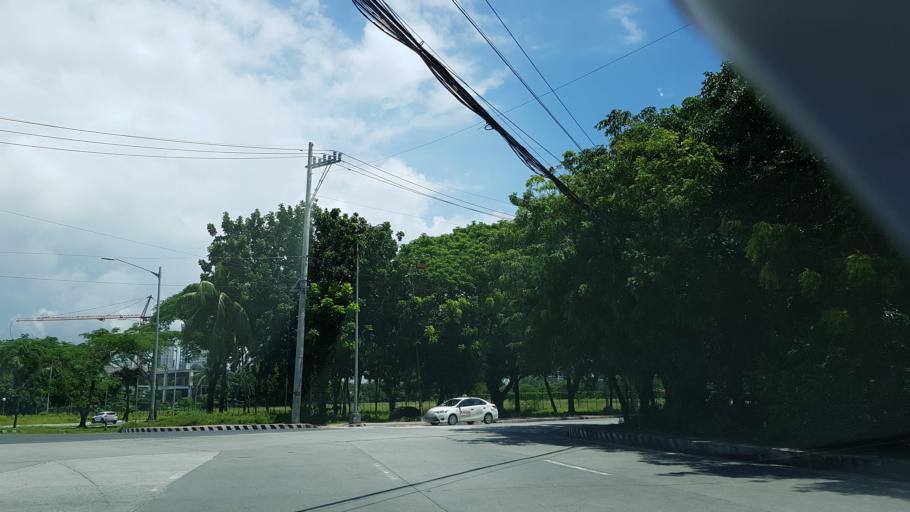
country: PH
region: Metro Manila
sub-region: City of Manila
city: Port Area
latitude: 14.5503
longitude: 120.9832
